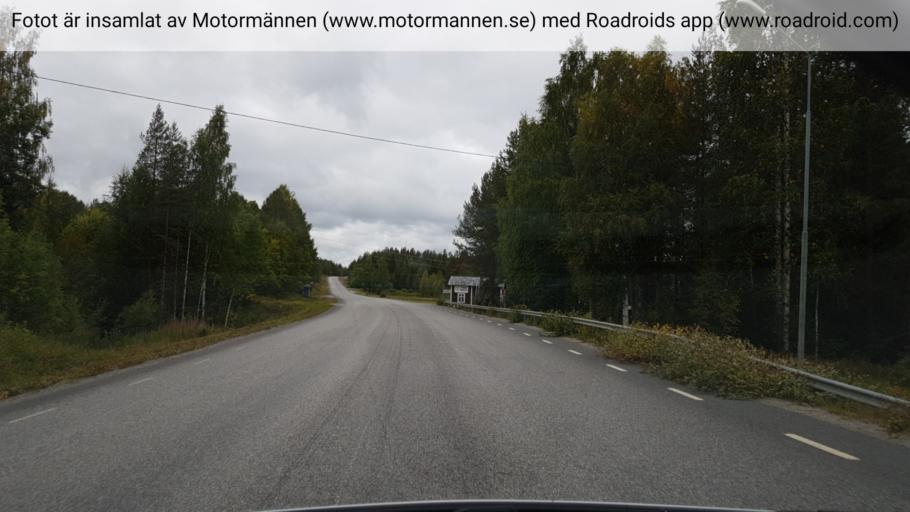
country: SE
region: Vaesterbotten
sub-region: Skelleftea Kommun
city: Langsele
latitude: 64.9250
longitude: 20.0386
